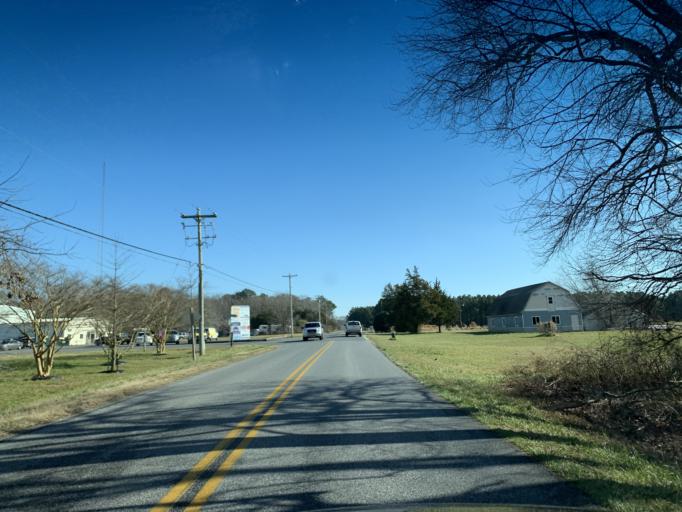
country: US
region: Maryland
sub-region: Worcester County
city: Ocean Pines
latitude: 38.4190
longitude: -75.1415
